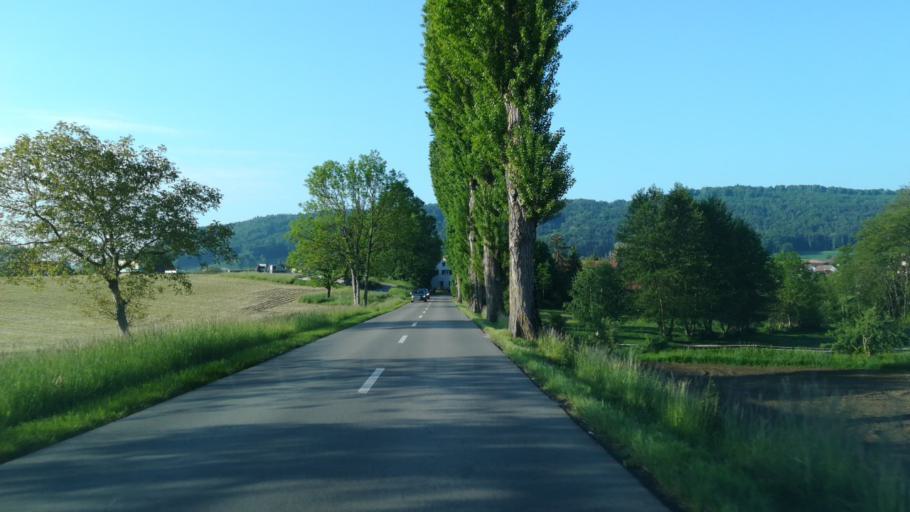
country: DE
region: Baden-Wuerttemberg
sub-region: Freiburg Region
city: Gottmadingen
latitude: 47.7218
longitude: 8.7872
